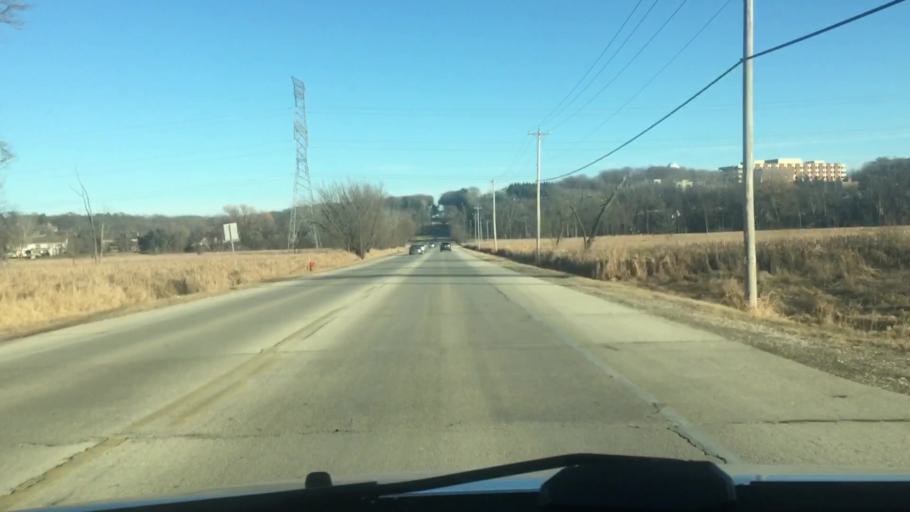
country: US
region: Wisconsin
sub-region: Waukesha County
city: Brookfield
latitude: 43.0614
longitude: -88.1634
